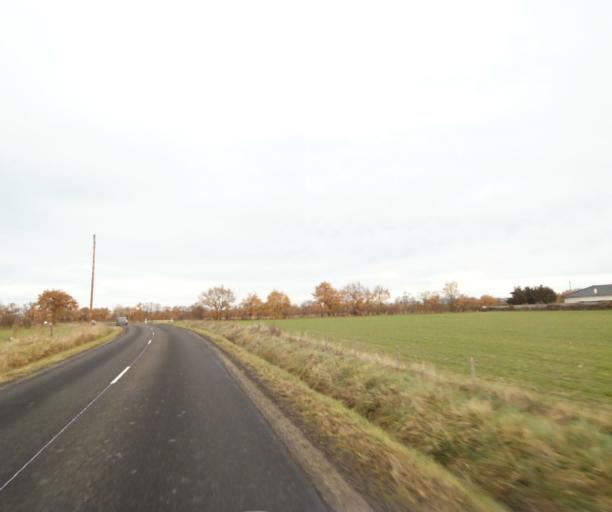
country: FR
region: Rhone-Alpes
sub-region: Departement de la Loire
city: Sury-le-Comtal
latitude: 45.5275
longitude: 4.1594
